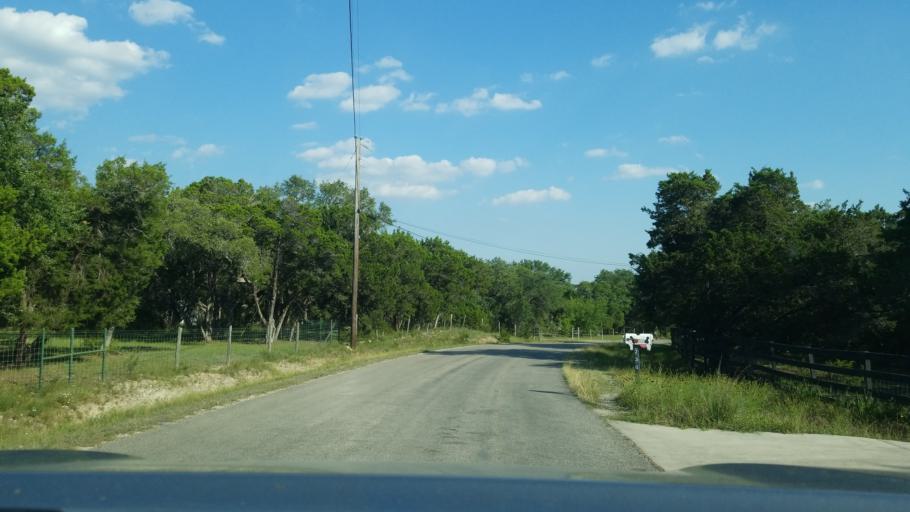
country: US
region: Texas
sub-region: Comal County
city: Bulverde
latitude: 29.7913
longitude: -98.4281
